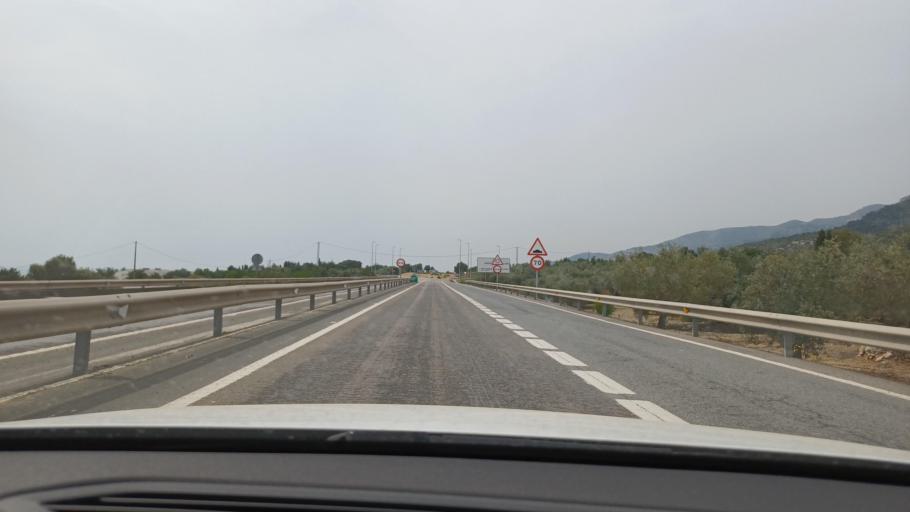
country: ES
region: Catalonia
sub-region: Provincia de Tarragona
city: Sant Carles de la Rapita
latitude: 40.6246
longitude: 0.5777
